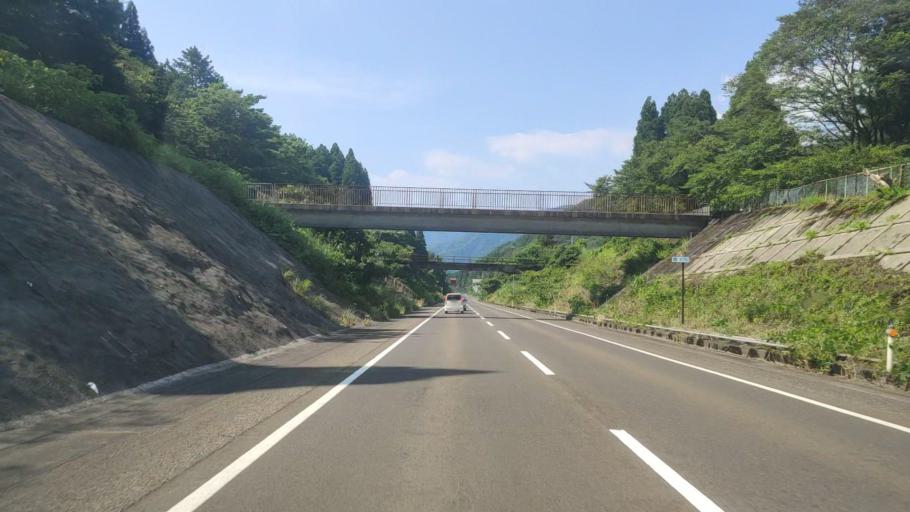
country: JP
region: Fukui
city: Tsuruga
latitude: 35.5861
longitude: 136.1243
